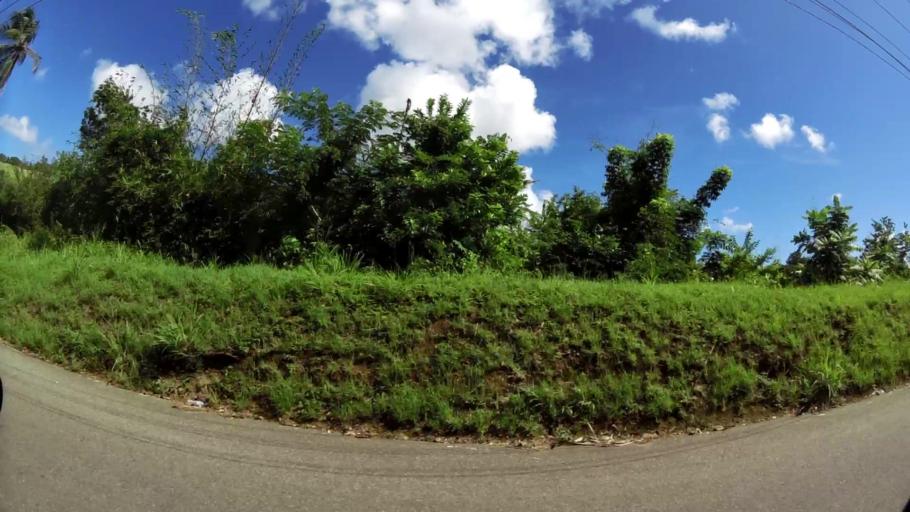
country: TT
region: Tobago
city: Scarborough
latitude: 11.1883
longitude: -60.7882
